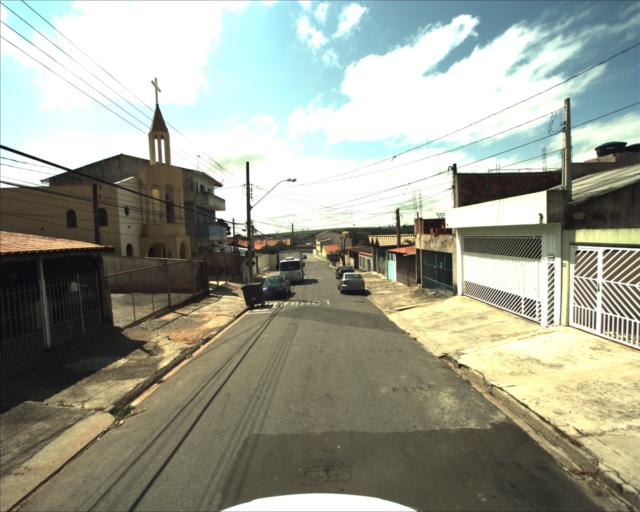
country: BR
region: Sao Paulo
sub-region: Sorocaba
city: Sorocaba
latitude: -23.3958
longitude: -47.3764
